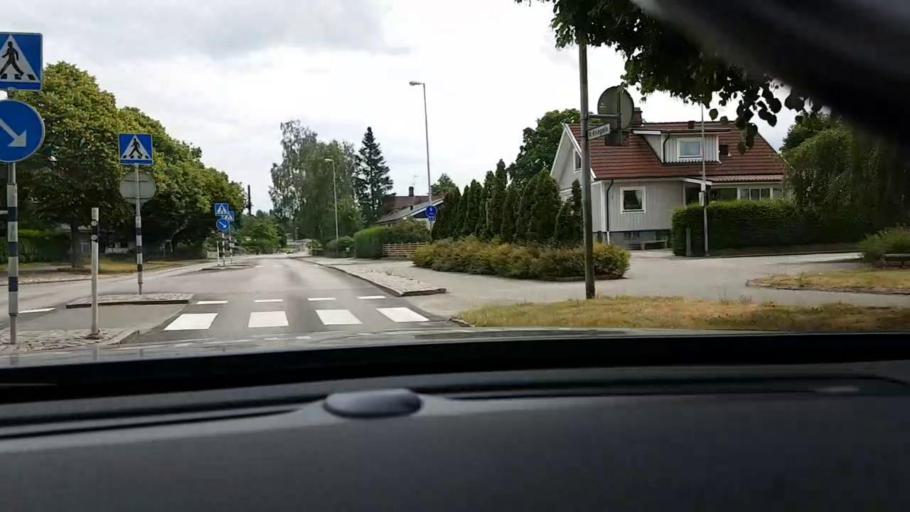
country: SE
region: Skane
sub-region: Hassleholms Kommun
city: Hassleholm
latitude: 56.1685
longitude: 13.7832
